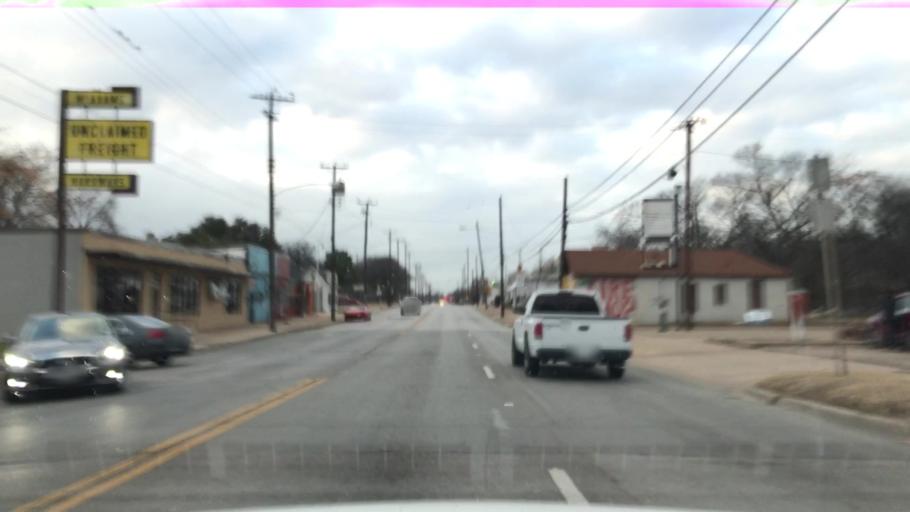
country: US
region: Texas
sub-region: Dallas County
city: Dallas
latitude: 32.7628
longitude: -96.7467
